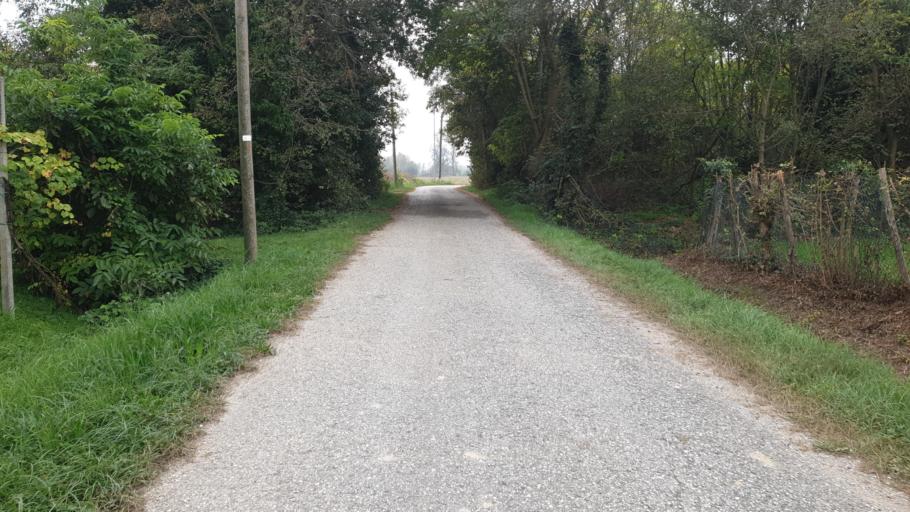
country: IT
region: Veneto
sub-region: Provincia di Padova
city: Casalserugo
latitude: 45.2936
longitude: 11.9206
